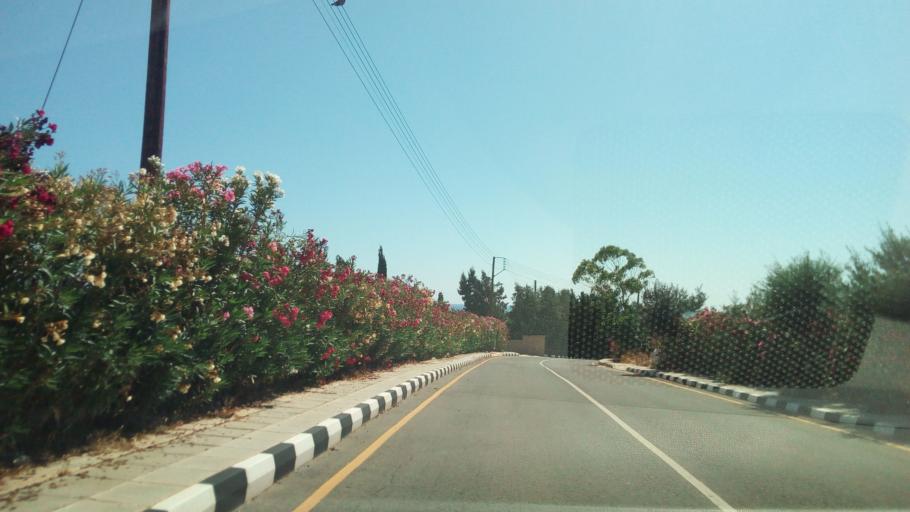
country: CY
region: Pafos
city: Pegeia
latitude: 34.8995
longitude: 32.3261
